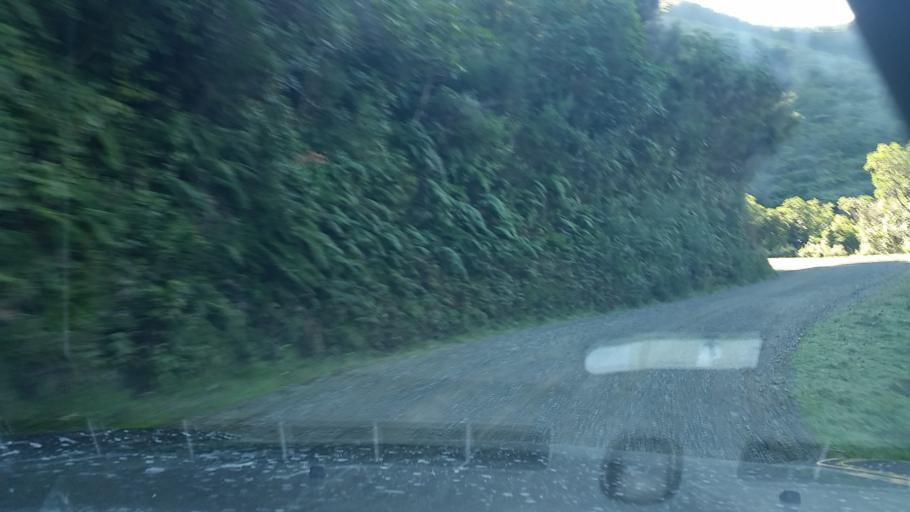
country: NZ
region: Marlborough
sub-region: Marlborough District
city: Picton
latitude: -41.1416
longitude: 174.0475
